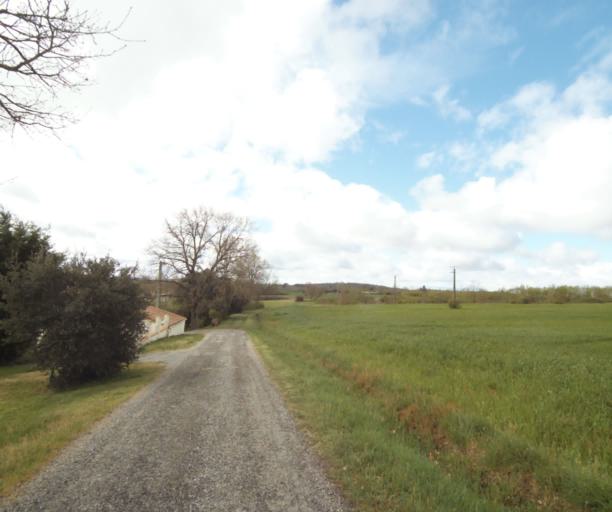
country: FR
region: Midi-Pyrenees
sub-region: Departement de l'Ariege
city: Saverdun
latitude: 43.2302
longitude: 1.5694
